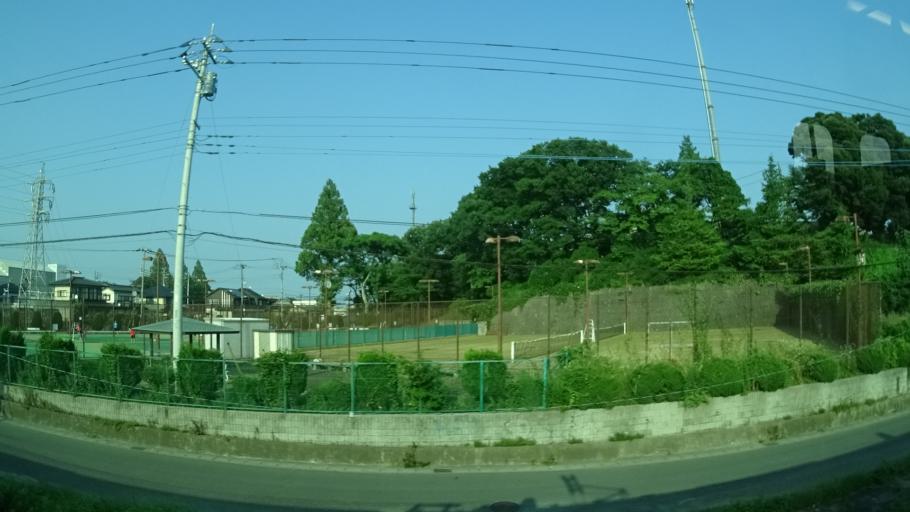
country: JP
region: Ibaraki
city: Hitachi
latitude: 36.6317
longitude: 140.6770
